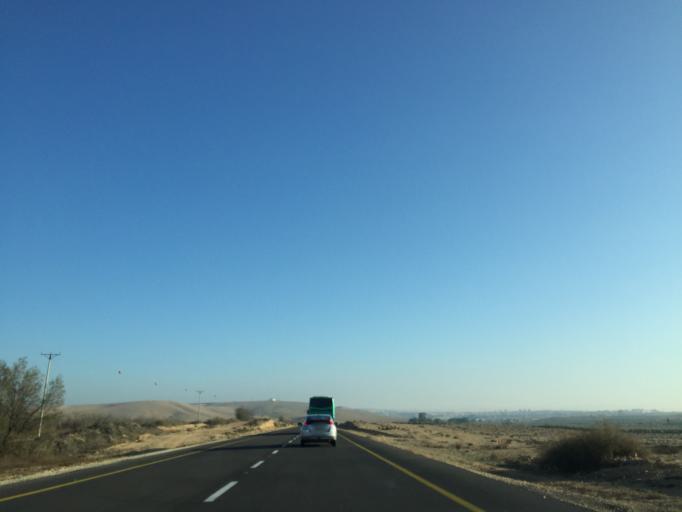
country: IL
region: Southern District
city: Dimona
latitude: 31.0427
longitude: 34.9795
